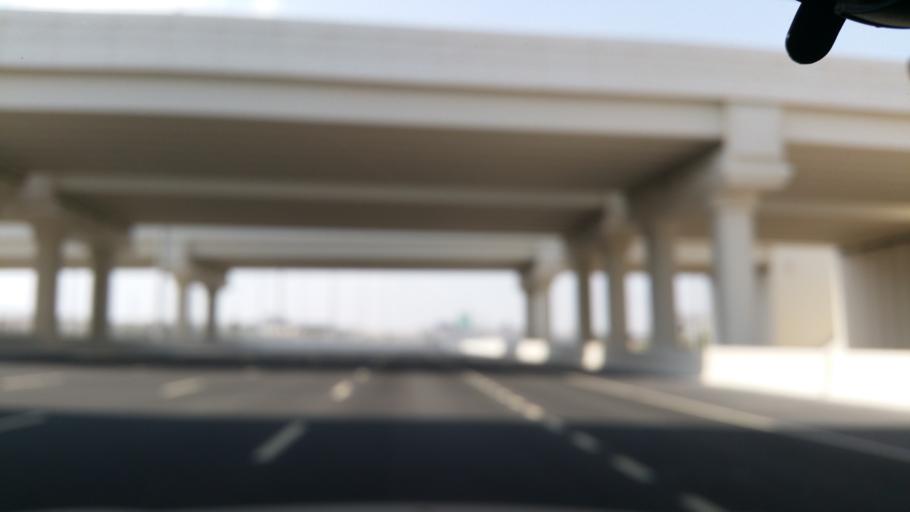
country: QA
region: Baladiyat Umm Salal
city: Umm Salal Muhammad
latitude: 25.4039
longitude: 51.4919
